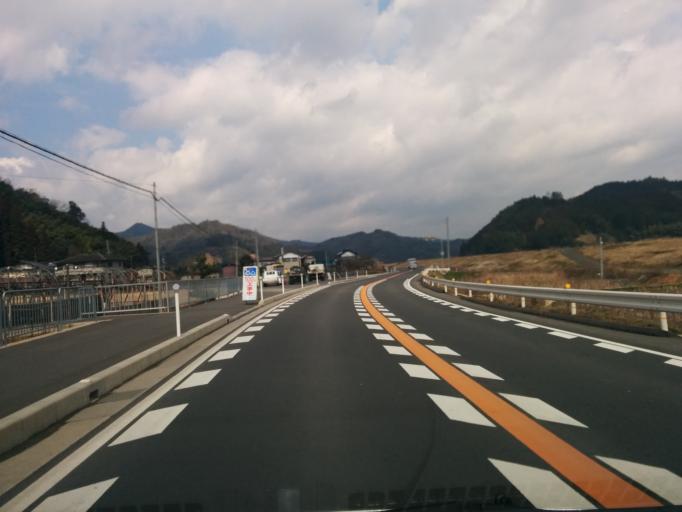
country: JP
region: Kyoto
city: Fukuchiyama
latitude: 35.3960
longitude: 135.1817
